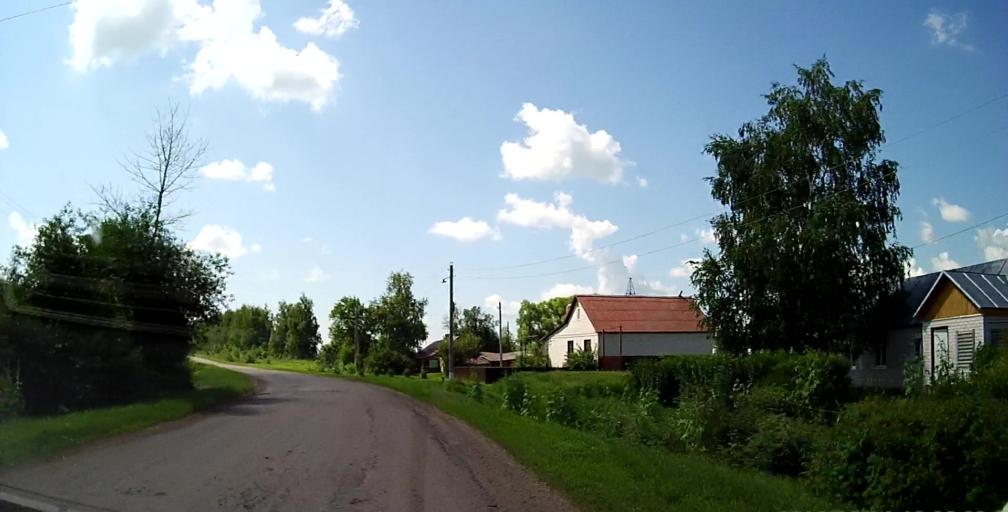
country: RU
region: Lipetsk
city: Chaplygin
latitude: 53.3689
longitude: 39.9162
